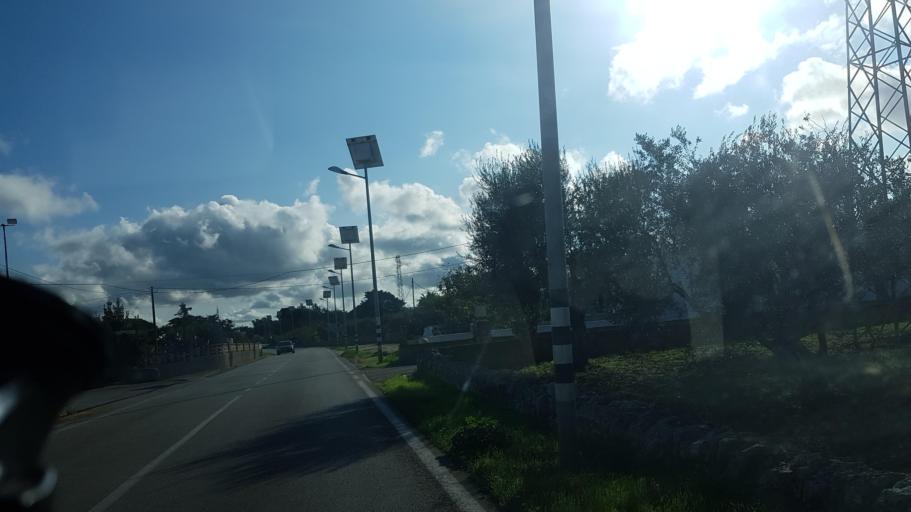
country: IT
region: Apulia
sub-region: Provincia di Brindisi
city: Ostuni
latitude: 40.7110
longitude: 17.5780
